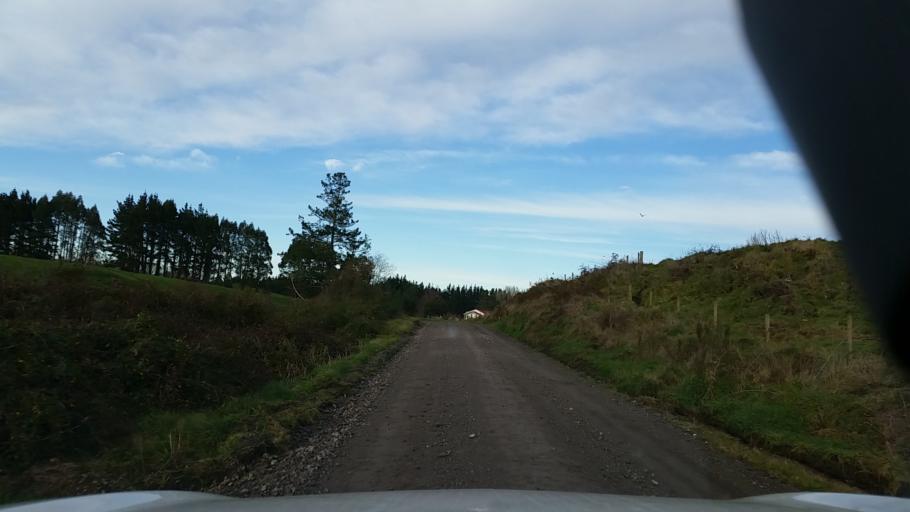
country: NZ
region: Bay of Plenty
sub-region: Rotorua District
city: Rotorua
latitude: -38.2631
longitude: 176.1593
